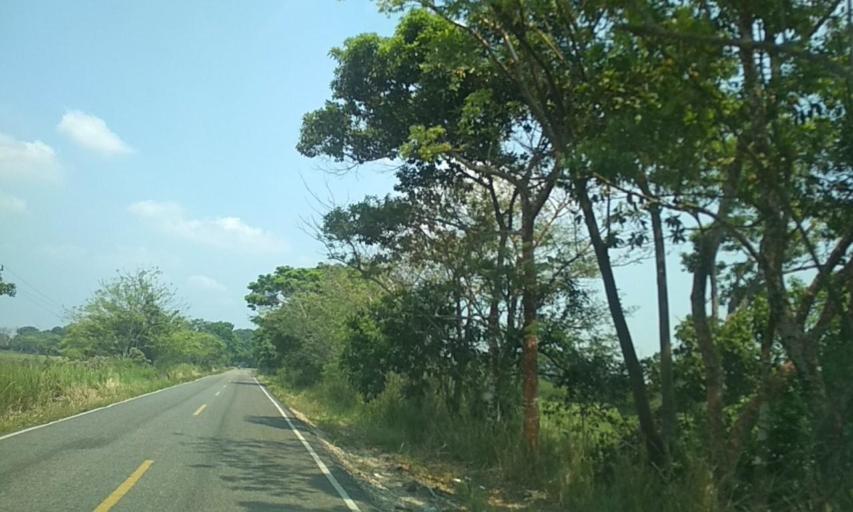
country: MX
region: Tabasco
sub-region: Huimanguillo
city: C-41 (Licenciado Carlos A. Madrazo)
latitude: 17.8497
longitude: -93.5323
